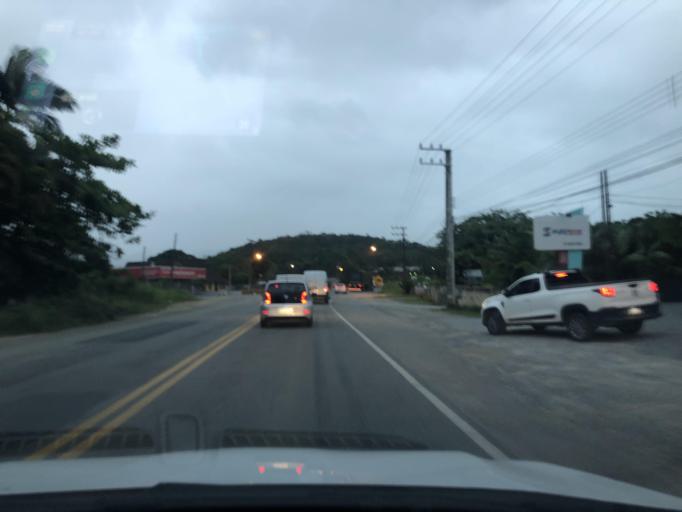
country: BR
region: Santa Catarina
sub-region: Pomerode
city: Pomerode
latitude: -26.7941
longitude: -49.0870
